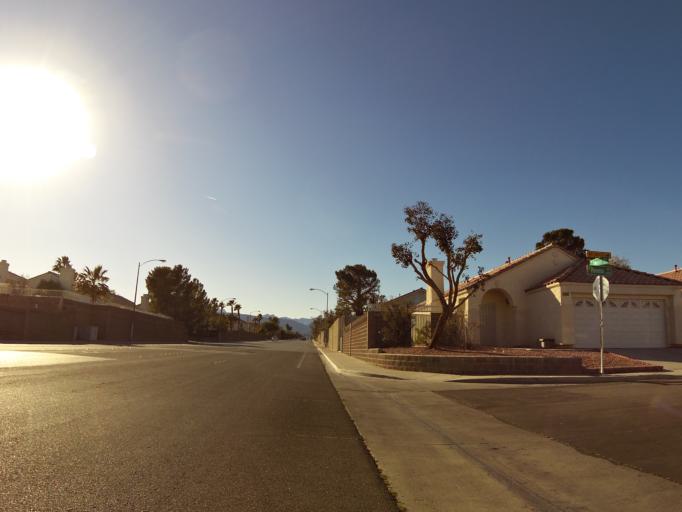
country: US
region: Nevada
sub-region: Clark County
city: Spring Valley
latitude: 36.1223
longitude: -115.2807
